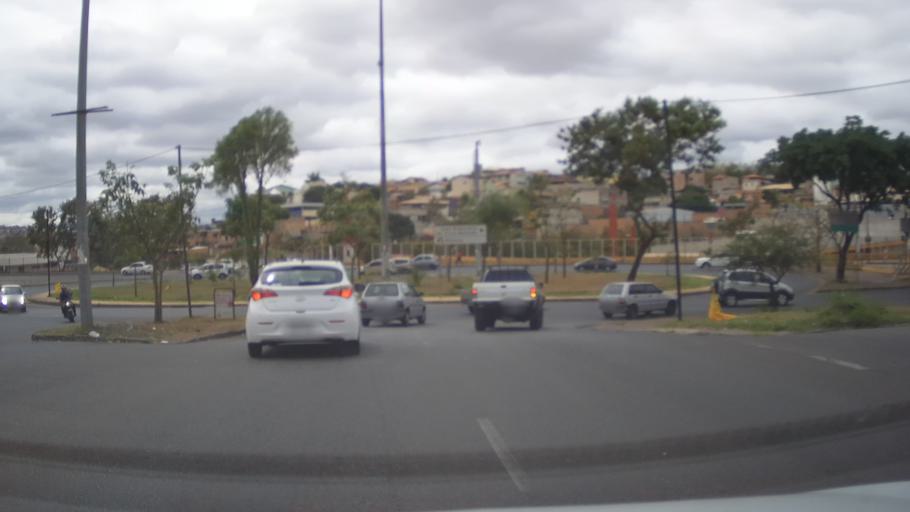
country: BR
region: Minas Gerais
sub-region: Belo Horizonte
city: Belo Horizonte
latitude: -19.8456
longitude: -43.9157
